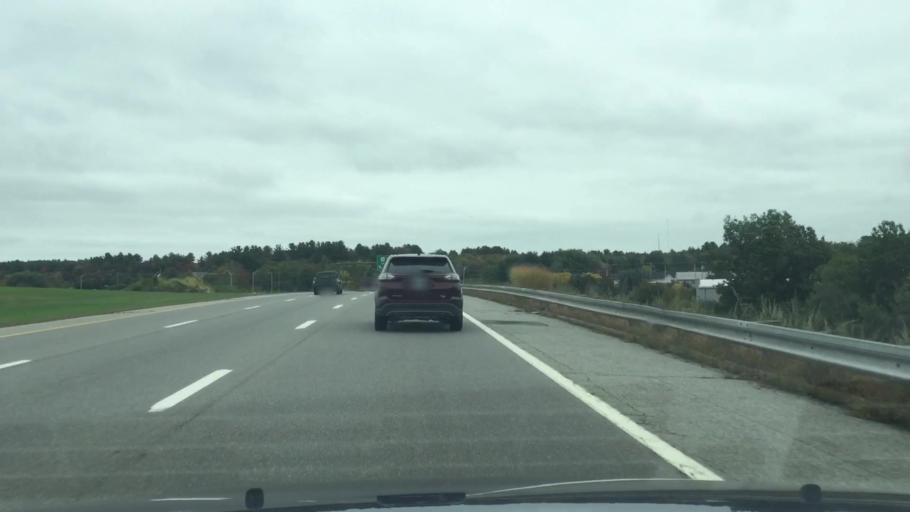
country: US
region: New Hampshire
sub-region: Hillsborough County
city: Hudson
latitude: 42.7267
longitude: -71.4293
